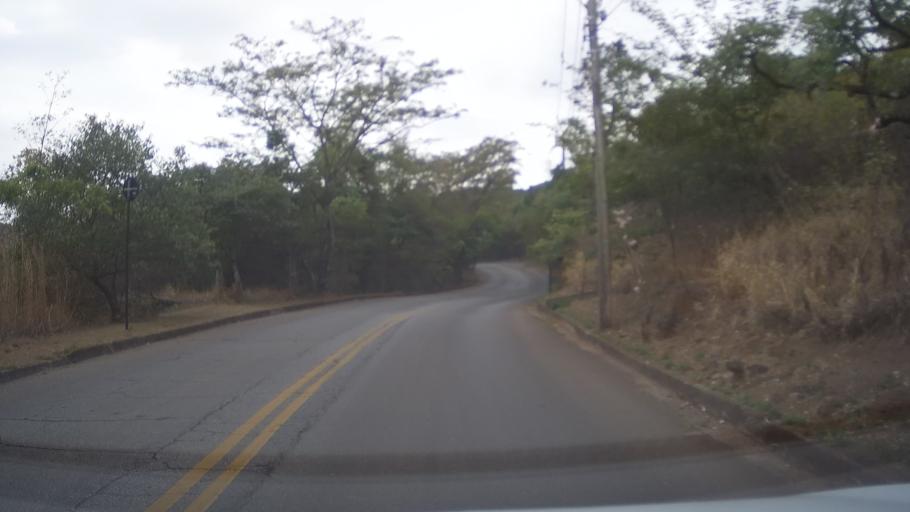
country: BR
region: Minas Gerais
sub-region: Belo Horizonte
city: Belo Horizonte
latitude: -19.9532
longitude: -43.9058
